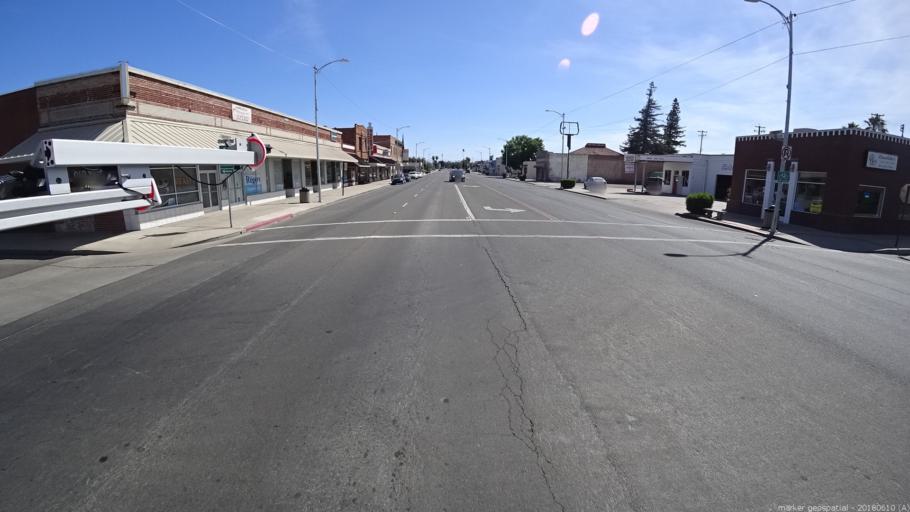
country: US
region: California
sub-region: Madera County
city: Chowchilla
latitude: 37.1222
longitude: -120.2610
